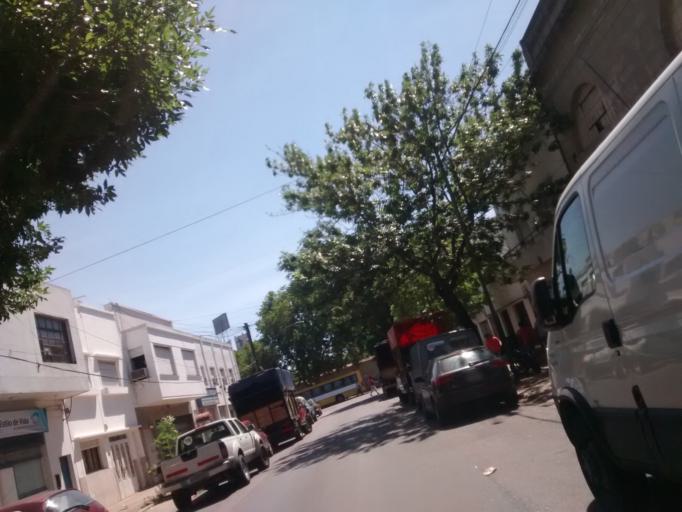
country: AR
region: Buenos Aires
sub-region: Partido de La Plata
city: La Plata
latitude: -34.9039
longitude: -57.9520
